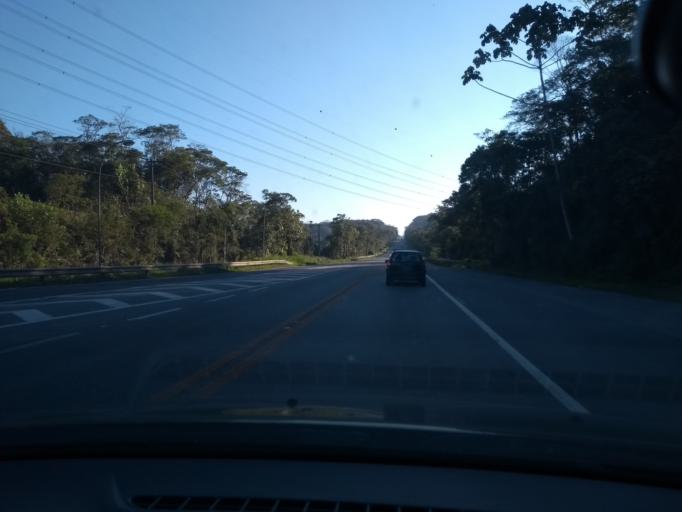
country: BR
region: Sao Paulo
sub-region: Rio Grande Da Serra
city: Rio Grande da Serra
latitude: -23.7710
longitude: -46.4736
